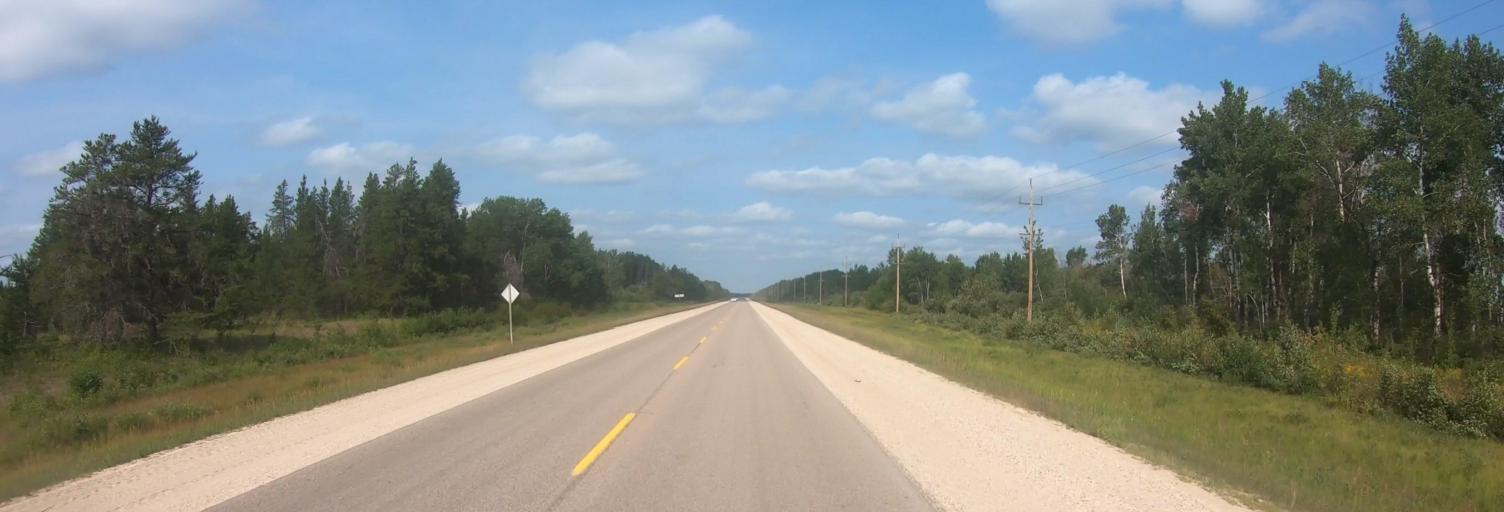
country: CA
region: Manitoba
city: La Broquerie
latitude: 49.2219
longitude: -96.3075
